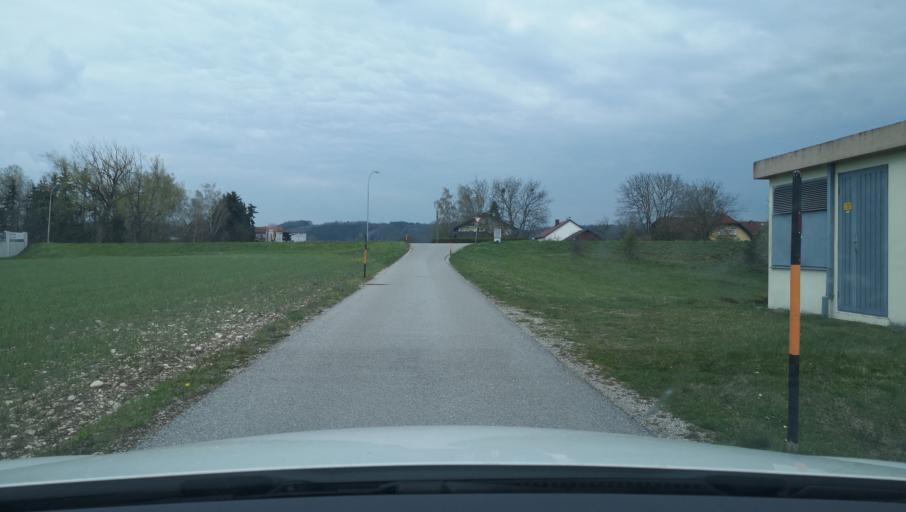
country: AT
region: Lower Austria
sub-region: Politischer Bezirk Amstetten
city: Euratsfeld
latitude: 48.1133
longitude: 14.9197
